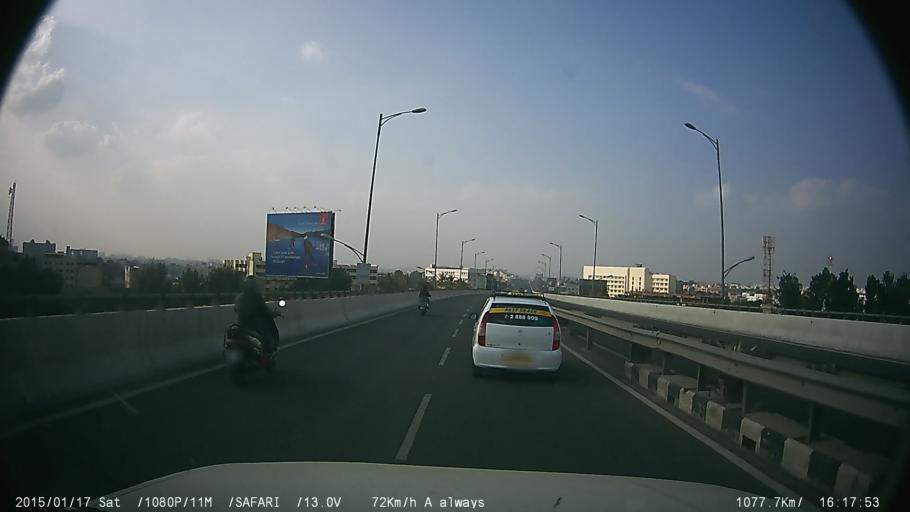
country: IN
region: Karnataka
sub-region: Bangalore Urban
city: Bangalore
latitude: 12.8762
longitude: 77.6480
